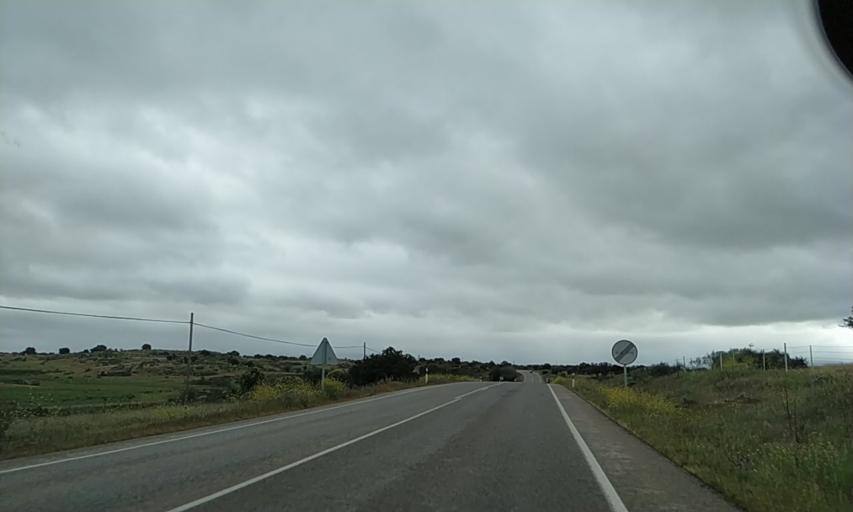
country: ES
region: Extremadura
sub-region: Provincia de Caceres
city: Caceres
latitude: 39.4094
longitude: -6.4164
